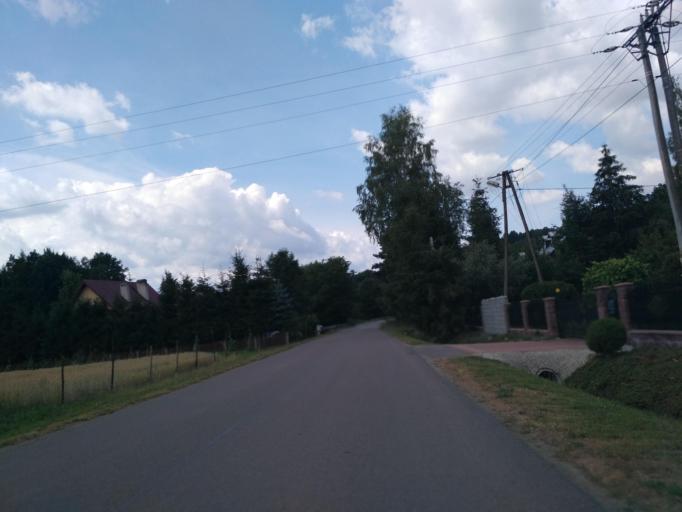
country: PL
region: Subcarpathian Voivodeship
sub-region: Powiat debicki
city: Brzostek
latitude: 49.9184
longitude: 21.3752
